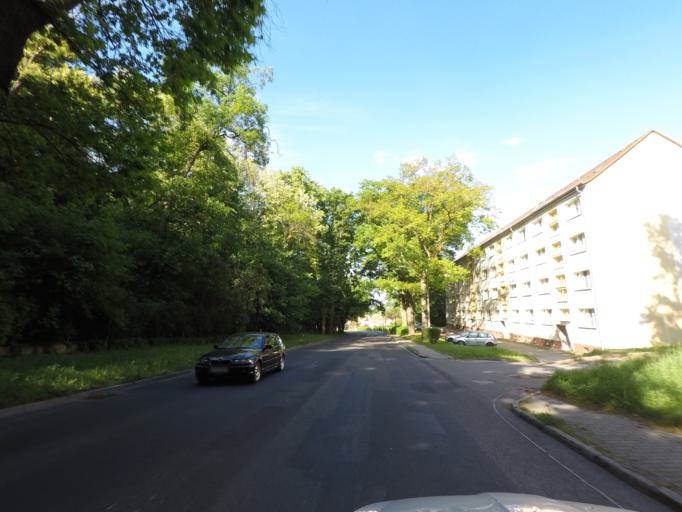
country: DE
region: Brandenburg
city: Bad Freienwalde
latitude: 52.7787
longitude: 14.0188
